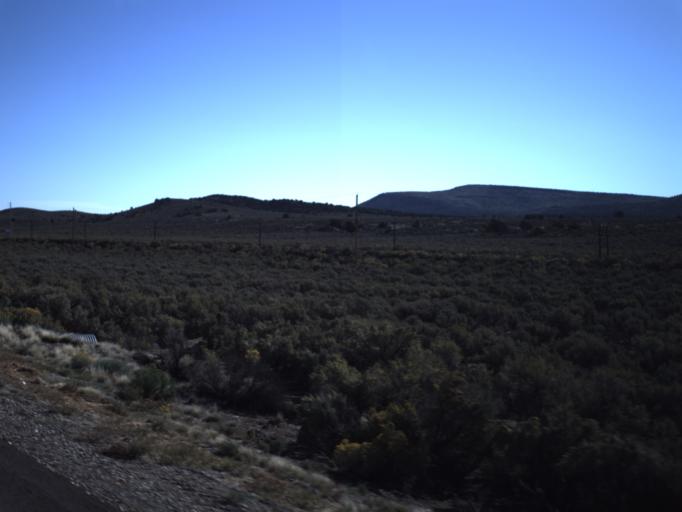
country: US
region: Utah
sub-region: Washington County
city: Enterprise
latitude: 37.7608
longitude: -113.9880
